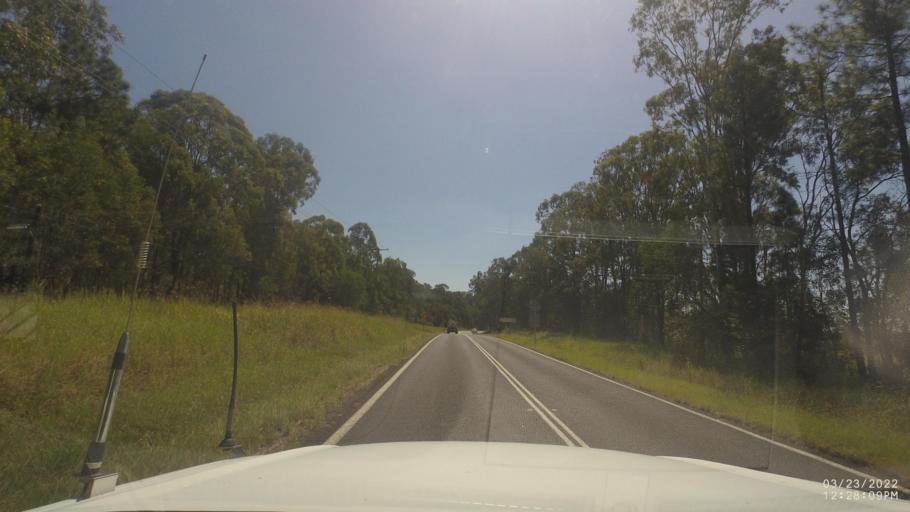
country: AU
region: Queensland
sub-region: Logan
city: Chambers Flat
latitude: -27.8181
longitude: 153.0983
